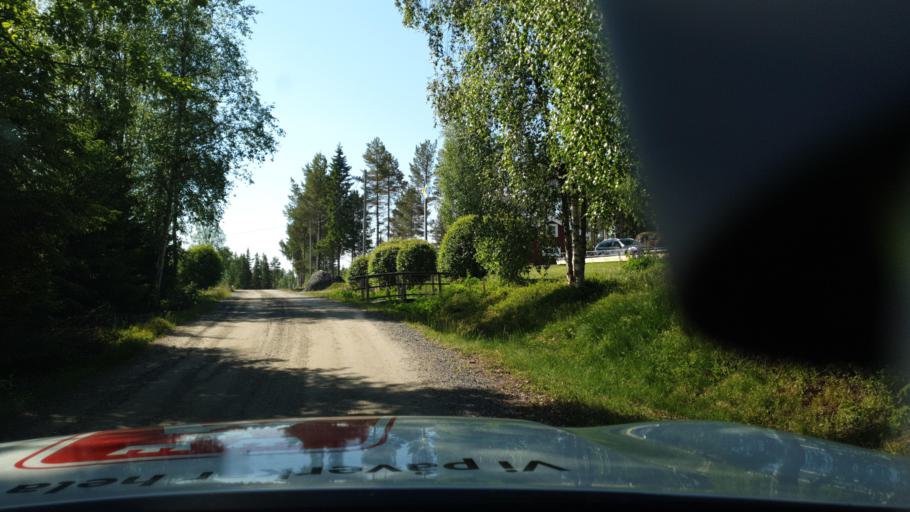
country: SE
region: Vaesterbotten
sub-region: Robertsfors Kommun
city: Robertsfors
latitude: 64.2122
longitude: 21.0778
